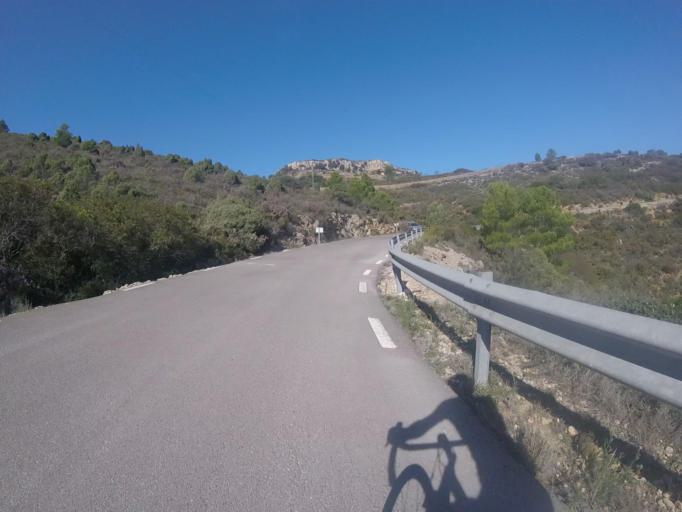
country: ES
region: Valencia
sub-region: Provincia de Castello
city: Sarratella
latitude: 40.2876
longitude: 0.0351
